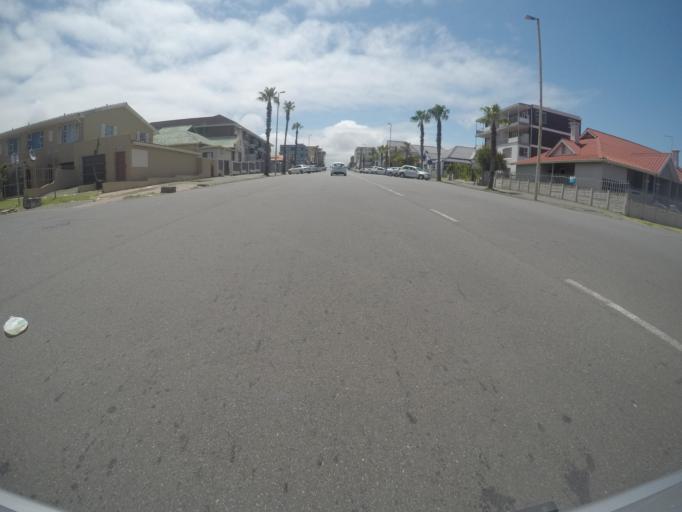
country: ZA
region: Eastern Cape
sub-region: Buffalo City Metropolitan Municipality
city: East London
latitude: -33.0208
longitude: 27.9142
